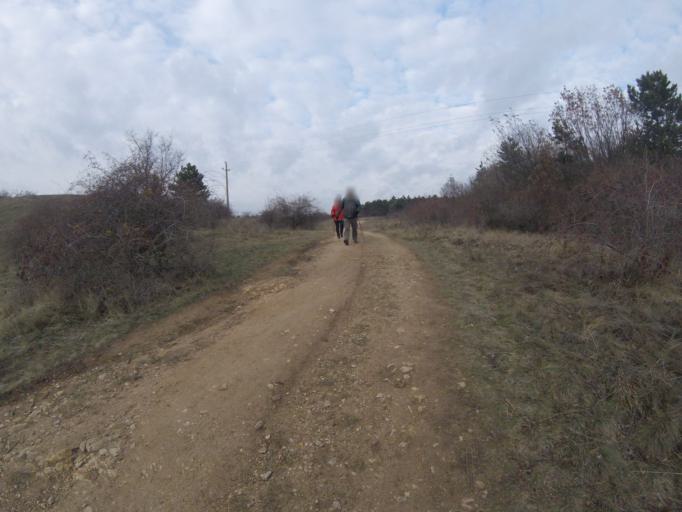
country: HU
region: Fejer
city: Velence
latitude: 47.2507
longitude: 18.6200
